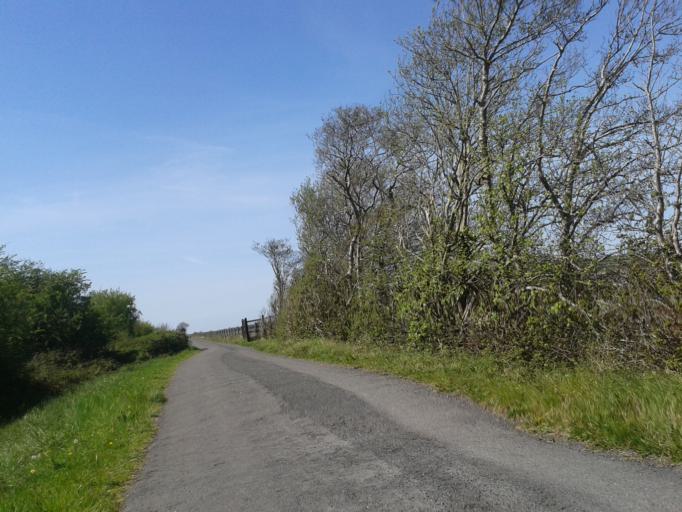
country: GB
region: England
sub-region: Devon
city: Barnstaple
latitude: 51.0766
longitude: -4.0760
